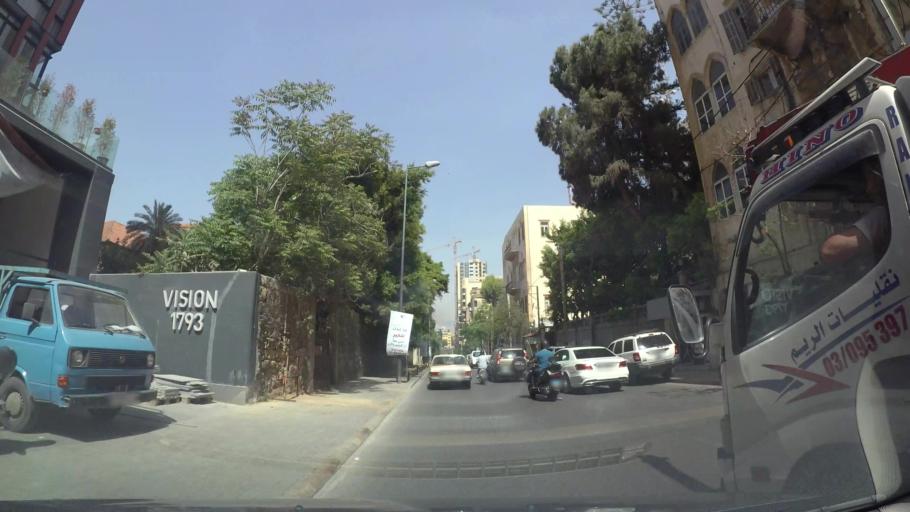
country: LB
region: Beyrouth
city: Beirut
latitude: 33.8946
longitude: 35.4922
